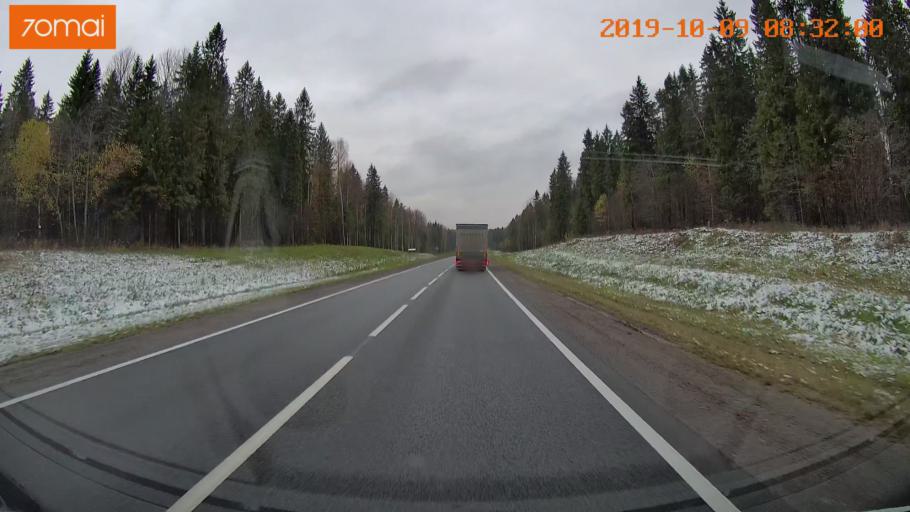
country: RU
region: Vologda
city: Gryazovets
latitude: 58.8610
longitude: 40.1988
